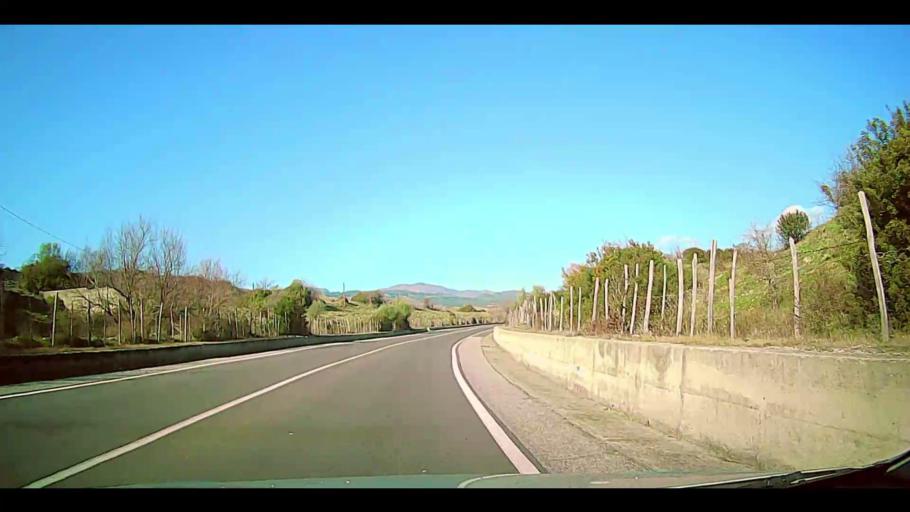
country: IT
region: Calabria
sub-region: Provincia di Crotone
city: Cotronei
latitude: 39.1860
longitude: 16.8203
